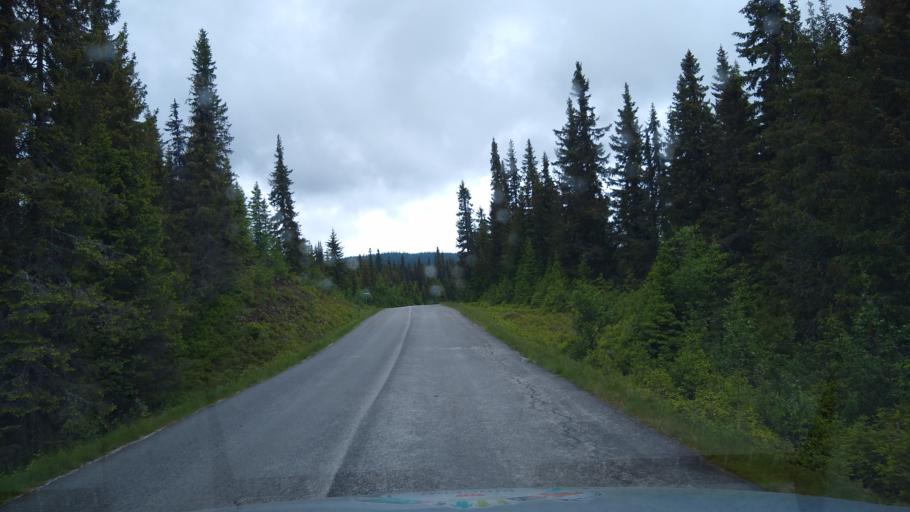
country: NO
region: Oppland
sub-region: Ringebu
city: Ringebu
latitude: 61.4880
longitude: 10.1135
